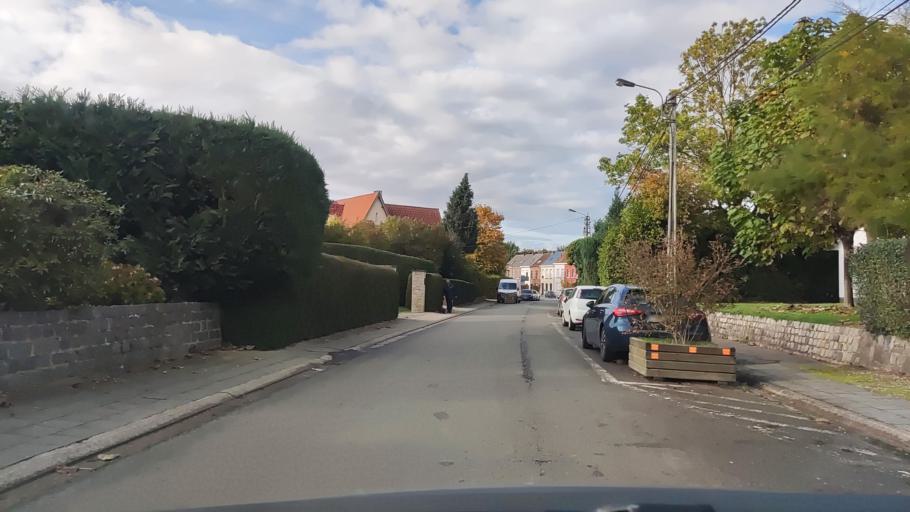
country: BE
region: Wallonia
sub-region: Province du Brabant Wallon
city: Jodoigne
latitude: 50.7183
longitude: 4.8736
